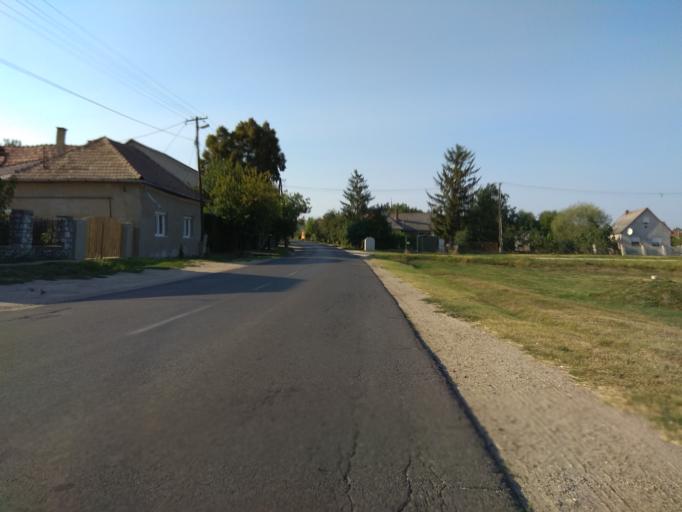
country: HU
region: Borsod-Abauj-Zemplen
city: Onod
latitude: 47.9993
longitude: 20.9199
